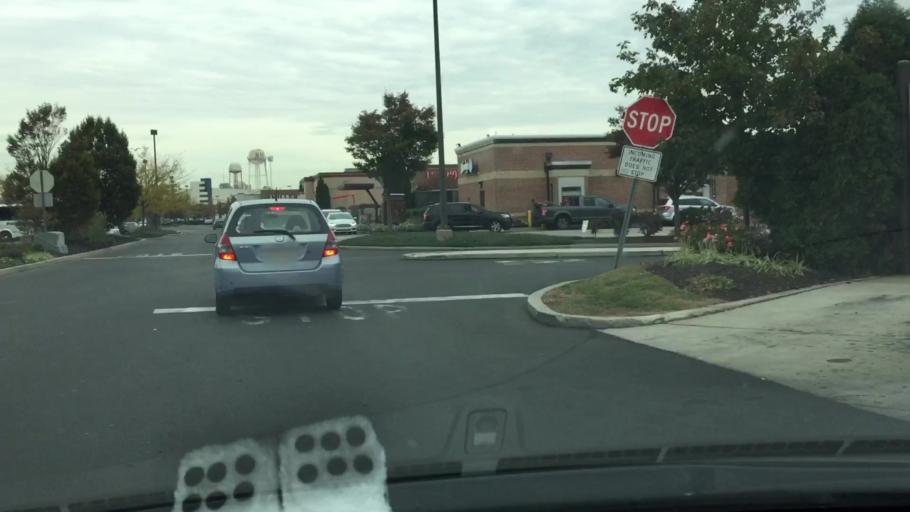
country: US
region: New Jersey
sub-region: Camden County
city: Camden
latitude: 39.9184
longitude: -75.1409
